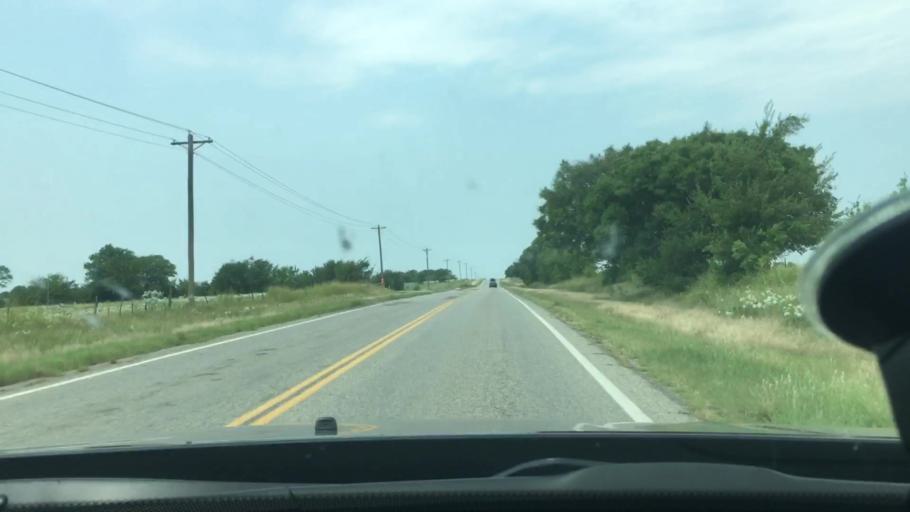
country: US
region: Oklahoma
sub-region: Marshall County
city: Kingston
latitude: 33.9983
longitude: -96.7673
